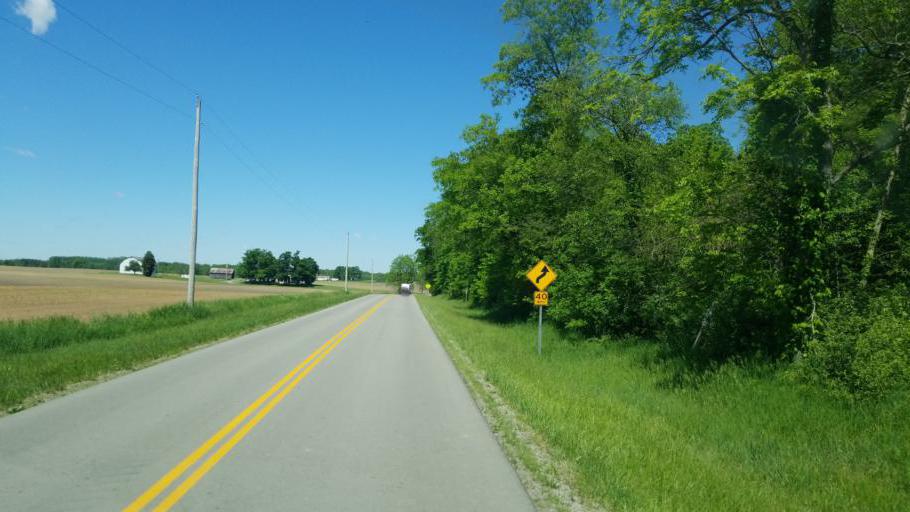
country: US
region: Ohio
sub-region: Logan County
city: Russells Point
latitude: 40.4175
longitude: -83.8988
